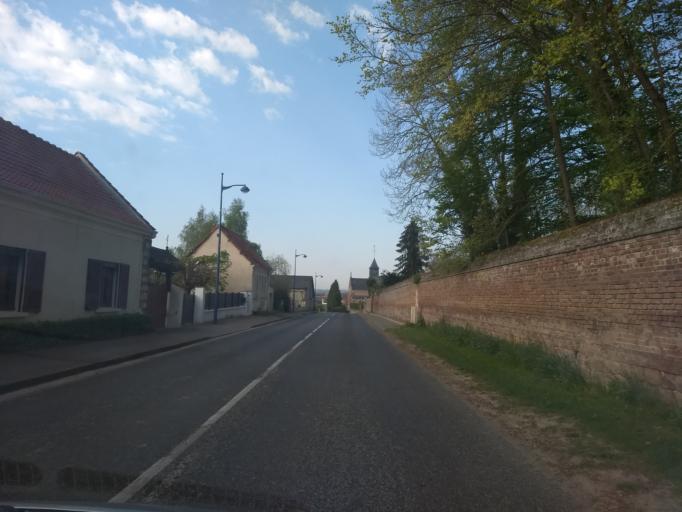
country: FR
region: Picardie
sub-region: Departement de la Somme
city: Corbie
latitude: 49.9888
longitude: 2.4461
